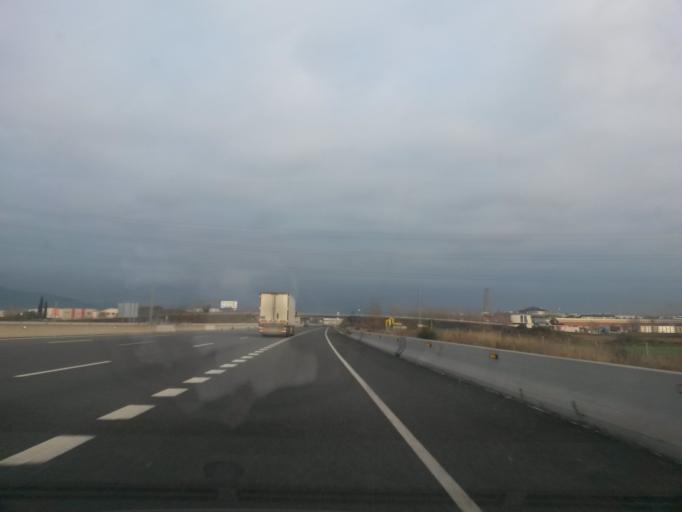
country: ES
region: Catalonia
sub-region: Provincia de Girona
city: Vilablareix
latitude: 41.9620
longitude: 2.7819
